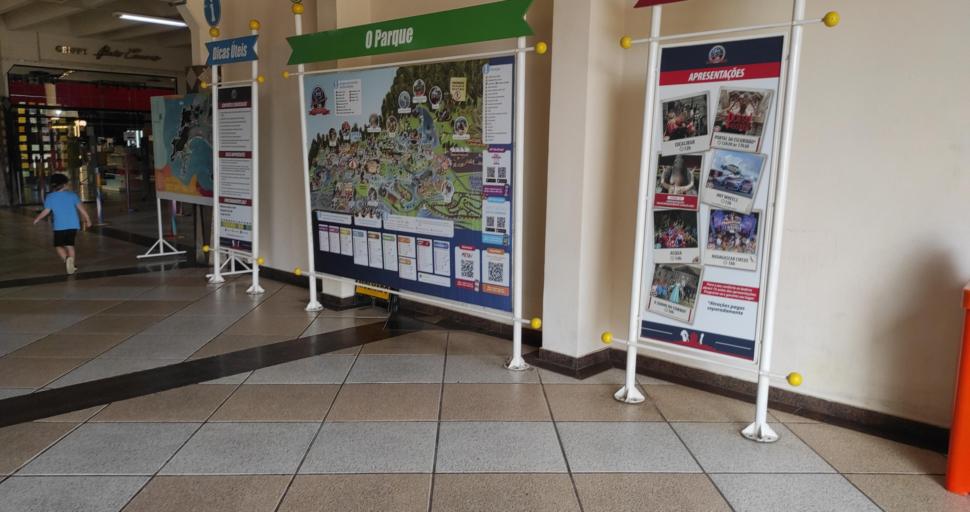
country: BR
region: Santa Catarina
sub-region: Penha
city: Penha
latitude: -26.7998
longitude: -48.6137
